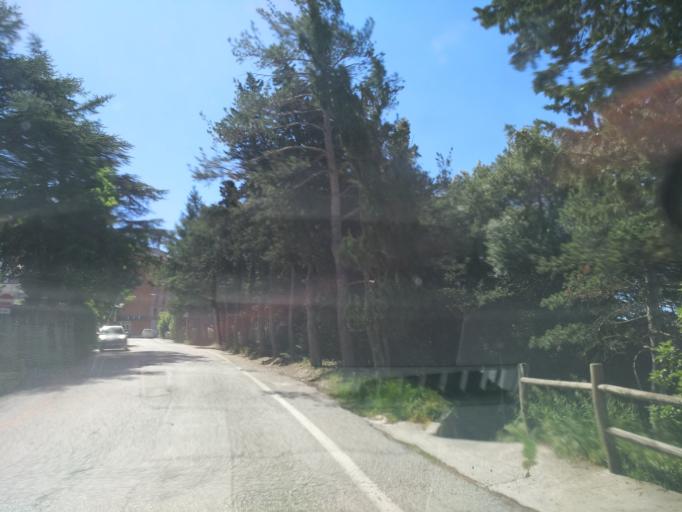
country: IT
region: The Marches
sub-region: Provincia di Pesaro e Urbino
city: Urbino
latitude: 43.7350
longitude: 12.6306
